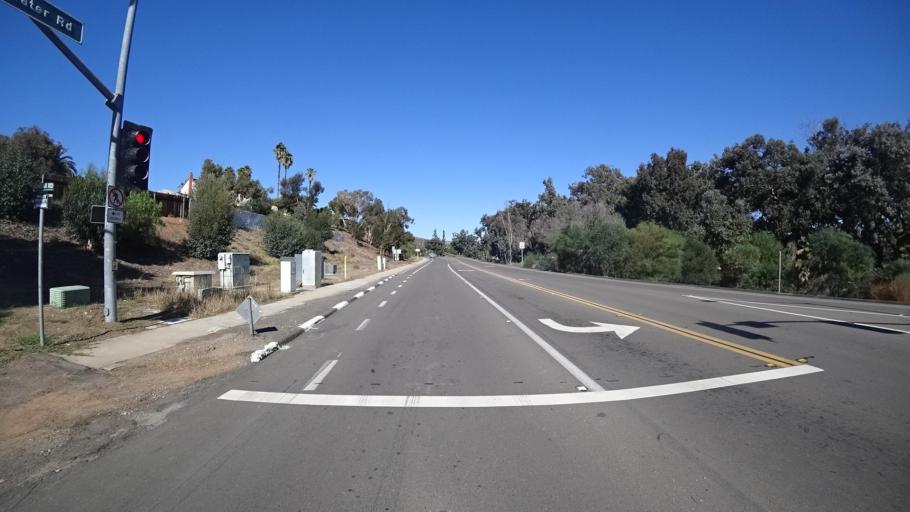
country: US
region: California
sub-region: San Diego County
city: Bonita
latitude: 32.6781
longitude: -117.0177
